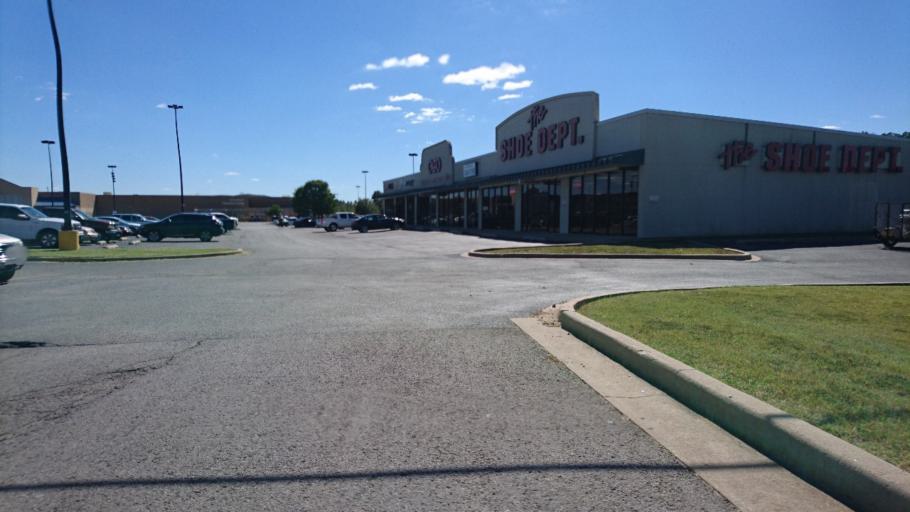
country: US
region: Oklahoma
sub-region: Creek County
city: Sapulpa
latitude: 35.9883
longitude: -96.1360
